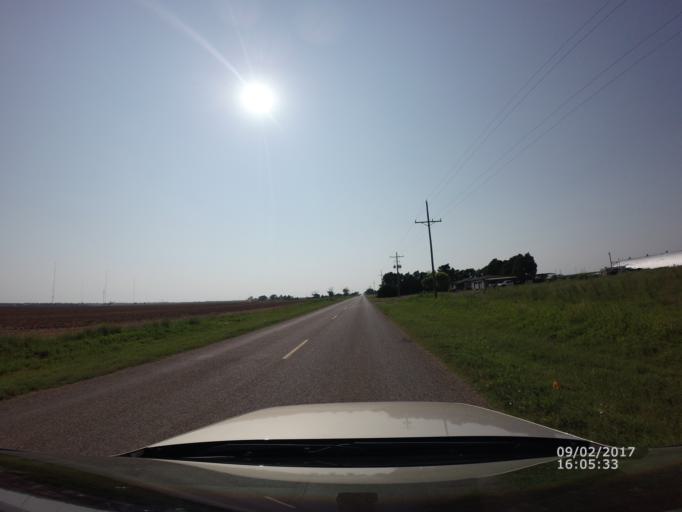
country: US
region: New Mexico
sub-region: Curry County
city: Clovis
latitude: 34.4483
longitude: -103.2019
